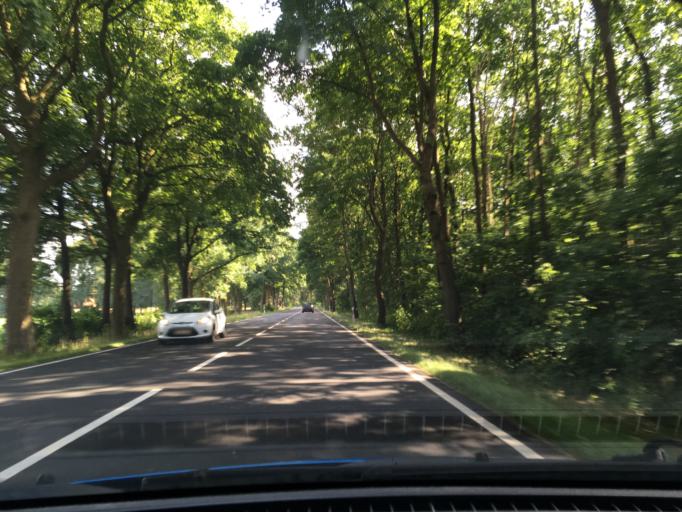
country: DE
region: Lower Saxony
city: Welle
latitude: 53.2281
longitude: 9.8060
